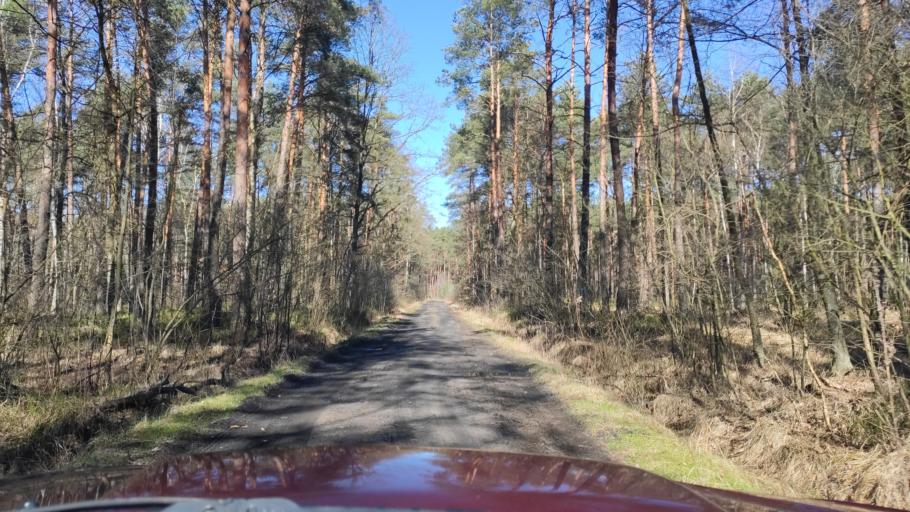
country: PL
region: Masovian Voivodeship
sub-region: Powiat kozienicki
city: Garbatka-Letnisko
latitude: 51.4334
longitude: 21.5471
